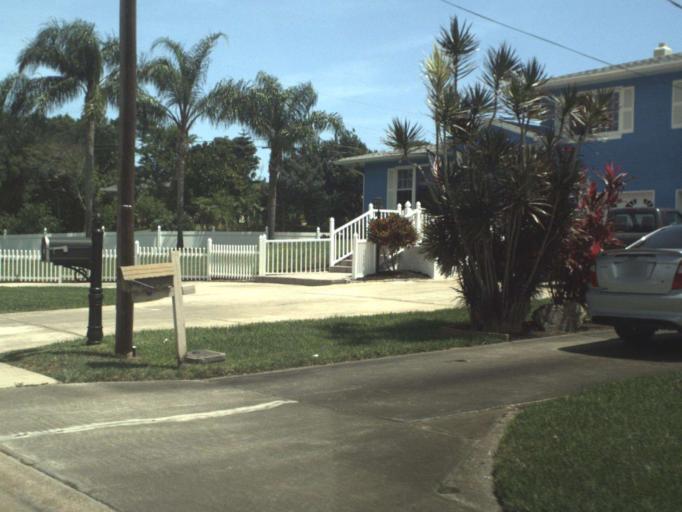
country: US
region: Florida
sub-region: Volusia County
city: Daytona Beach
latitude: 29.2015
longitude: -80.9999
